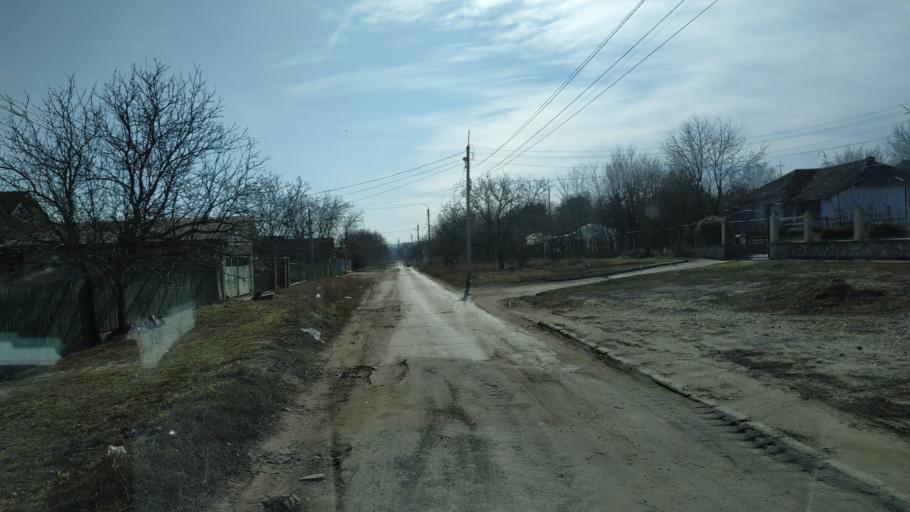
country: MD
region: Nisporeni
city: Nisporeni
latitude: 47.0678
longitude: 28.1738
